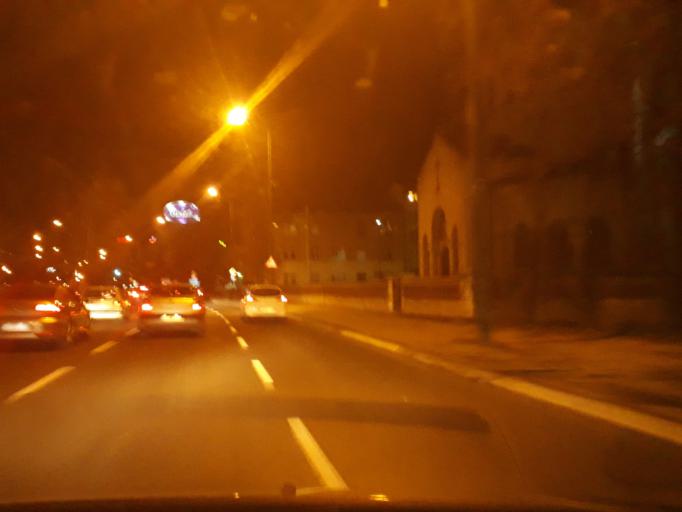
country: BA
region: Federation of Bosnia and Herzegovina
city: Kobilja Glava
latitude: 43.8534
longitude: 18.3904
